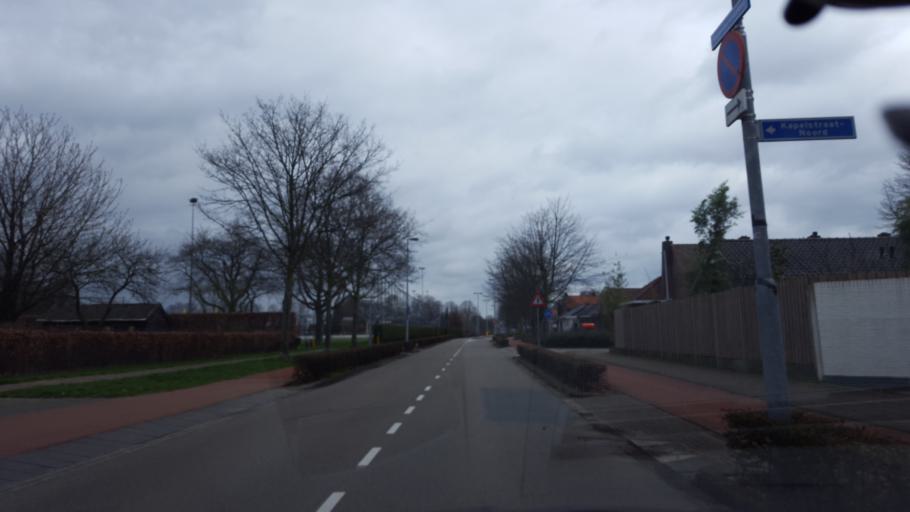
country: NL
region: North Brabant
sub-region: Gemeente Veldhoven
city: Veldhoven
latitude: 51.4187
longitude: 5.4134
